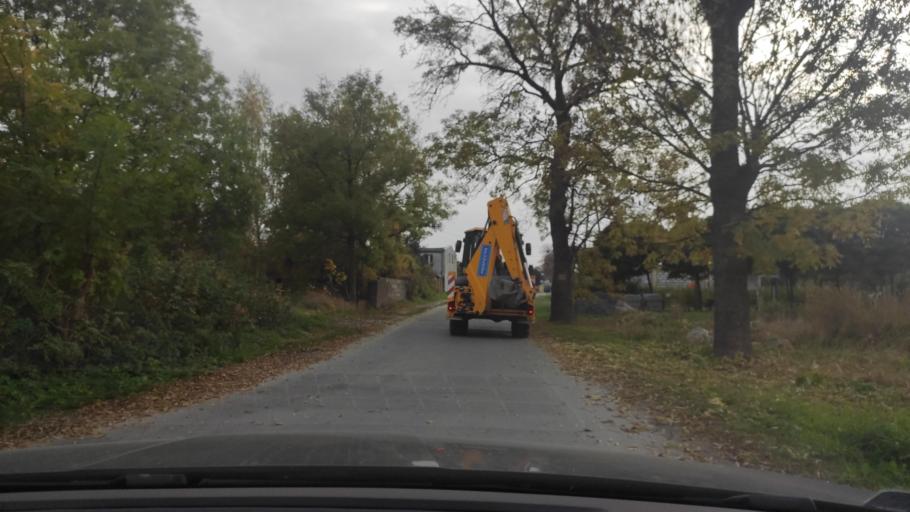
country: PL
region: Greater Poland Voivodeship
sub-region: Powiat poznanski
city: Kostrzyn
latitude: 52.4480
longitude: 17.2121
